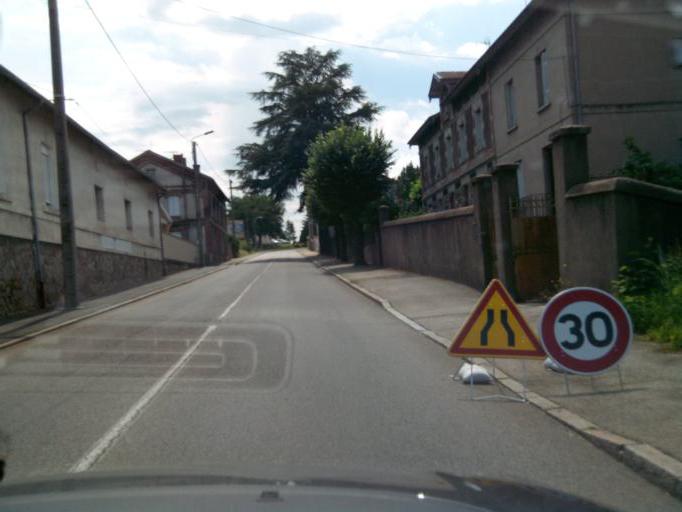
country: FR
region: Rhone-Alpes
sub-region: Departement de la Loire
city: La Ricamarie
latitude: 45.4213
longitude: 4.3144
